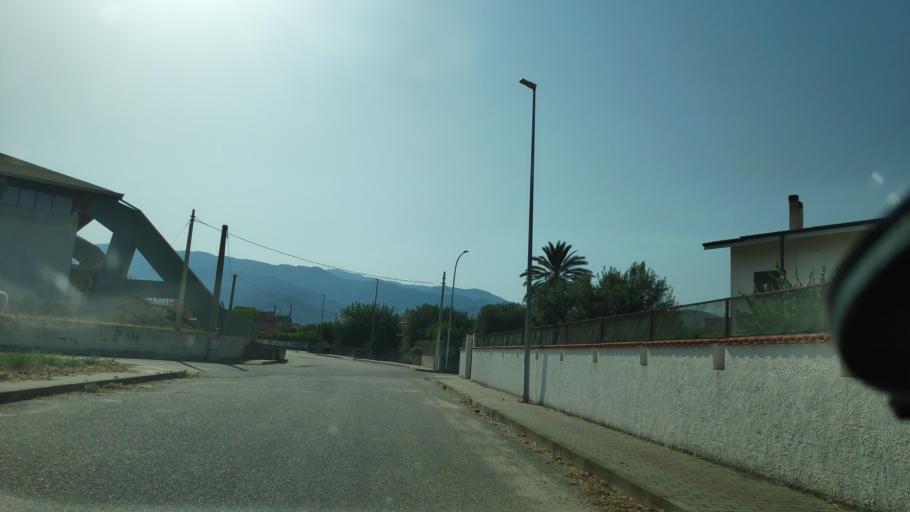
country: IT
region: Calabria
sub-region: Provincia di Catanzaro
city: Isca Marina
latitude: 38.6028
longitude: 16.5615
